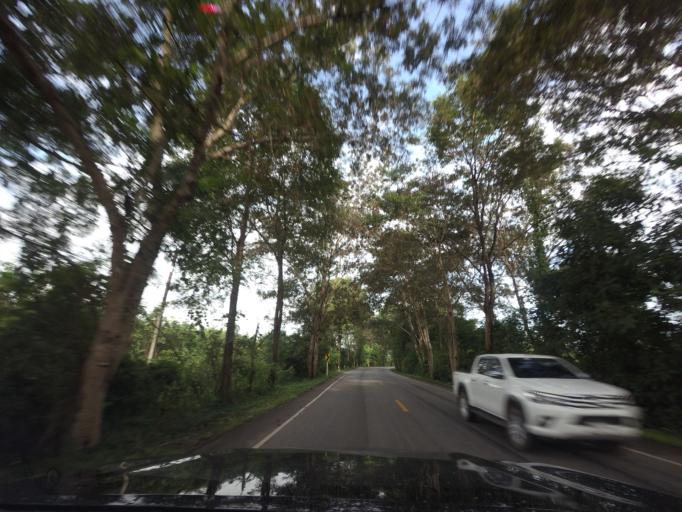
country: TH
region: Nong Khai
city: Pho Tak
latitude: 17.7893
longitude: 102.3620
